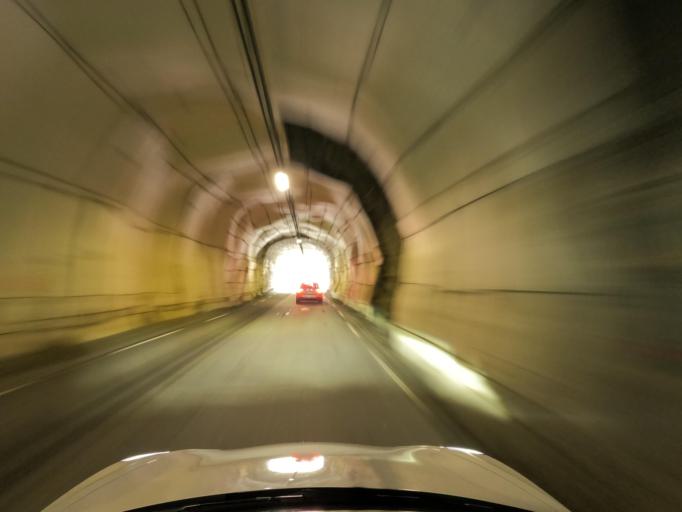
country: NO
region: Telemark
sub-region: Tinn
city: Rjukan
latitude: 59.8698
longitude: 8.4800
